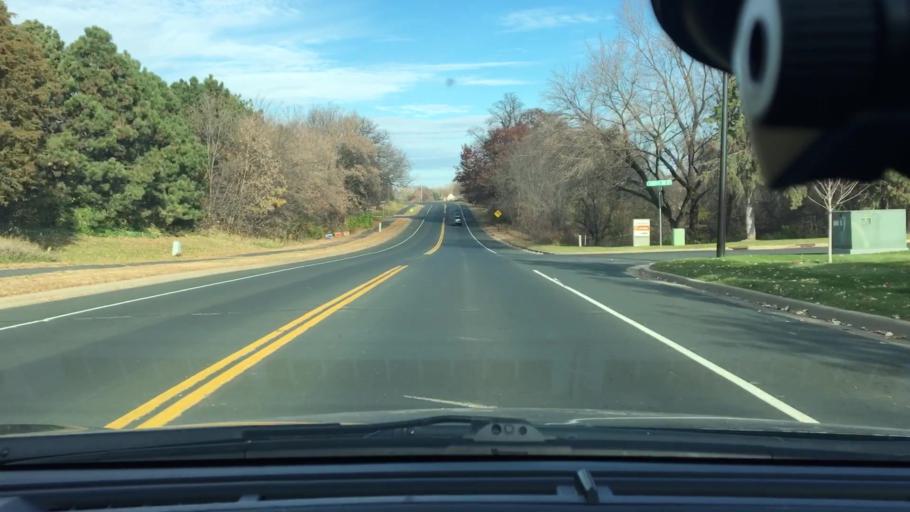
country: US
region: Minnesota
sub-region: Hennepin County
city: Maple Grove
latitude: 45.0984
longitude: -93.4555
